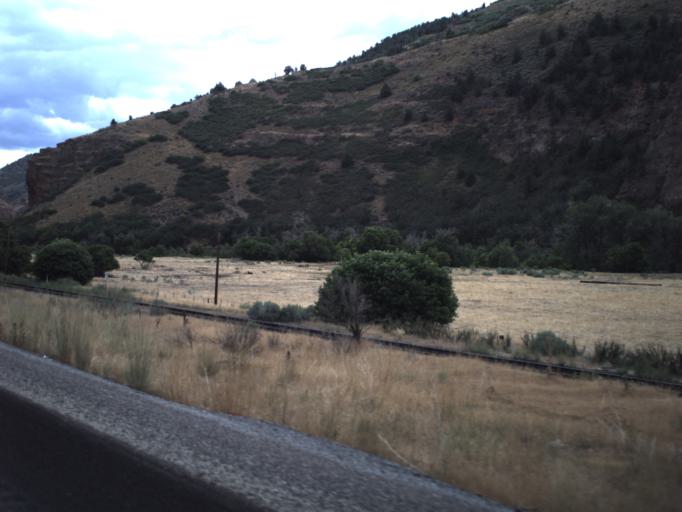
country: US
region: Utah
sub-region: Utah County
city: Mapleton
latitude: 39.9971
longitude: -111.4107
